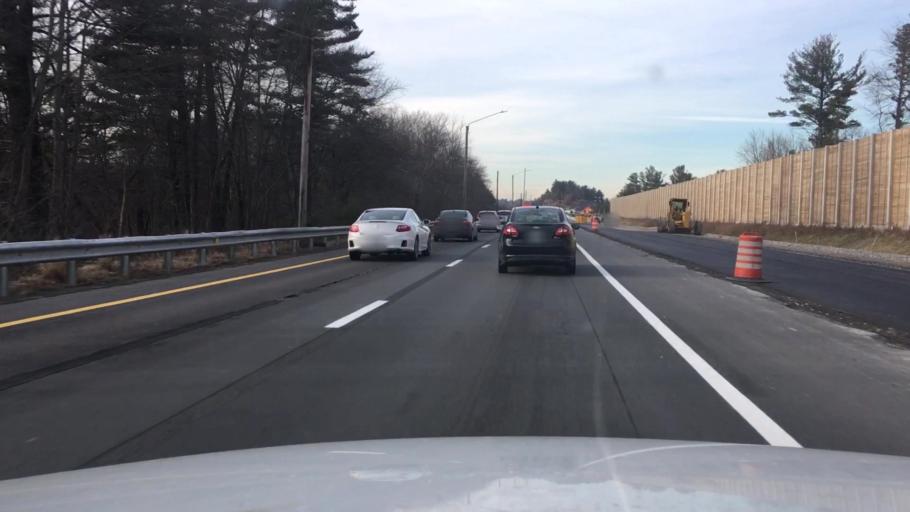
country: US
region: New Hampshire
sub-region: Hillsborough County
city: Manchester
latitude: 42.9506
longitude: -71.3980
